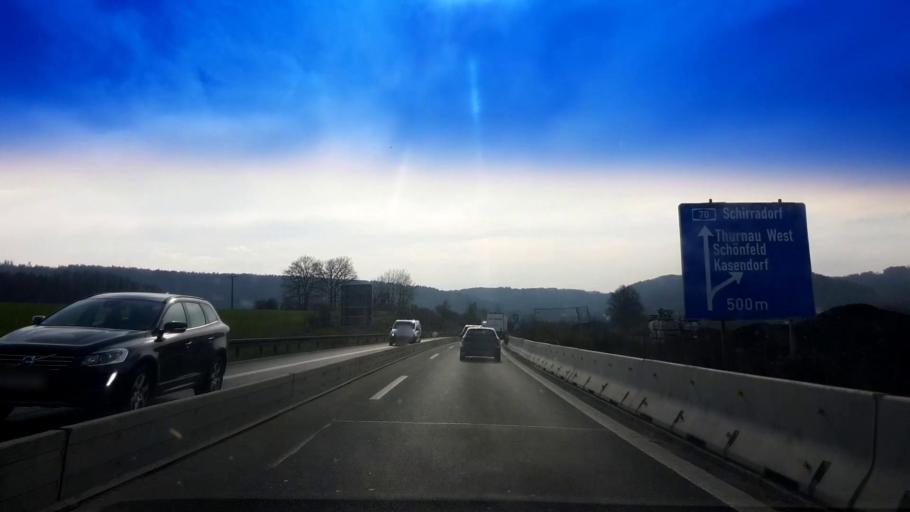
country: DE
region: Bavaria
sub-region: Upper Franconia
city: Thurnau
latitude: 50.0168
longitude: 11.3988
